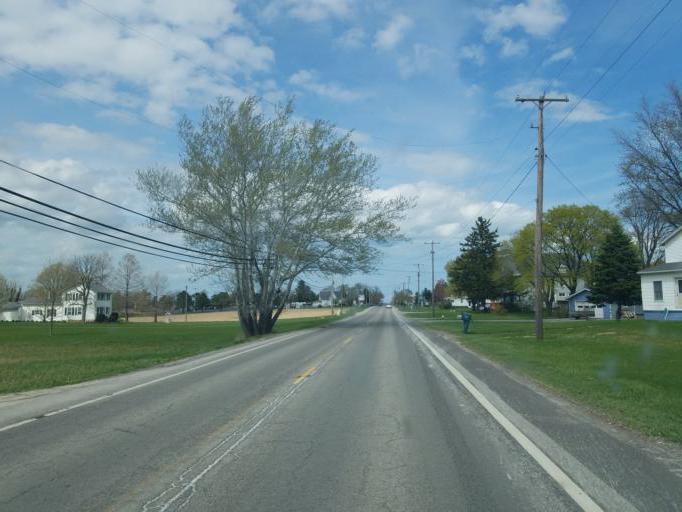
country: US
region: Ohio
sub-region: Erie County
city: Sandusky
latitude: 41.4130
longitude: -82.7245
